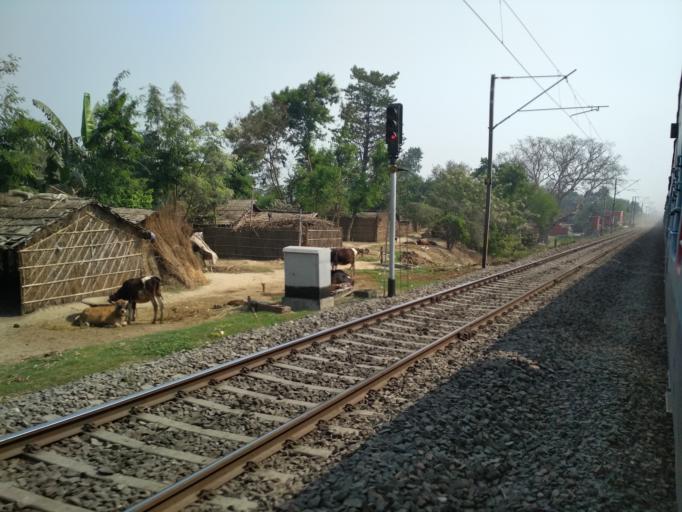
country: IN
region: Bihar
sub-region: Khagaria
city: Khagaria
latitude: 25.5072
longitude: 86.4940
